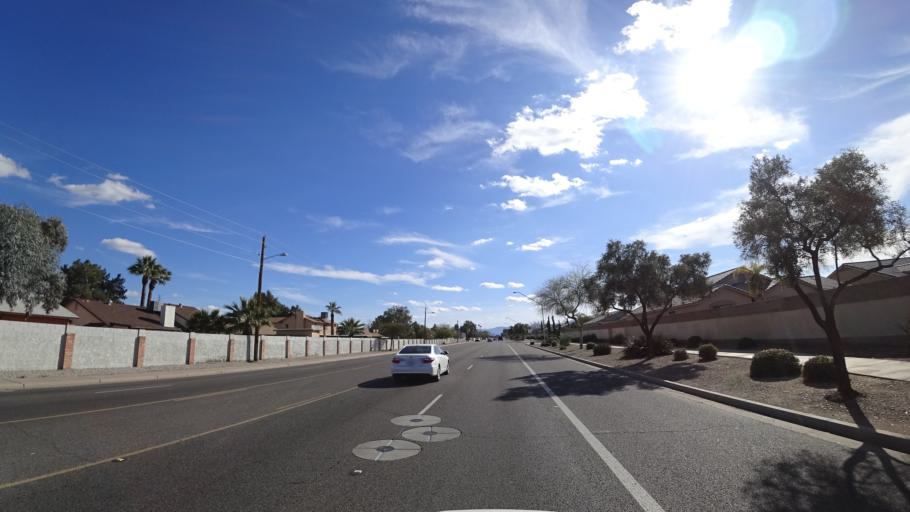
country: US
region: Arizona
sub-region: Maricopa County
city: Glendale
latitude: 33.5150
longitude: -112.2206
